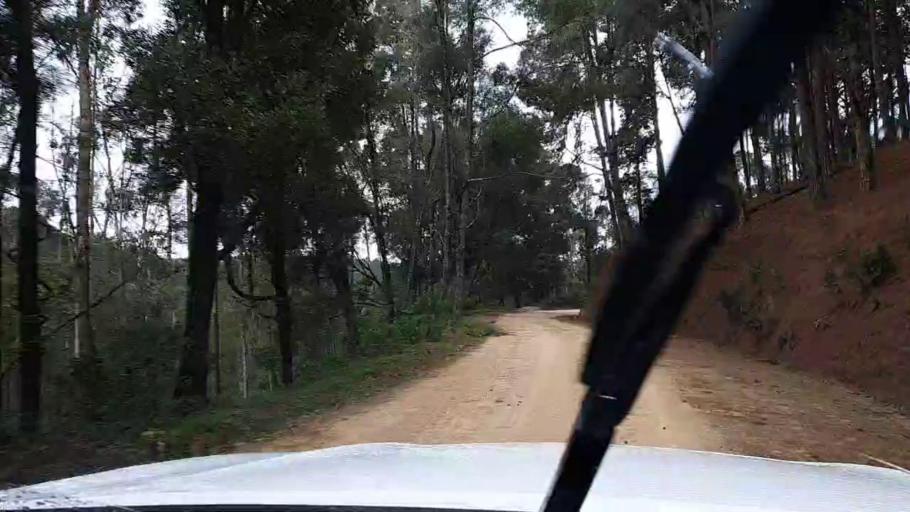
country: RW
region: Southern Province
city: Nzega
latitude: -2.3622
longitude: 29.3814
